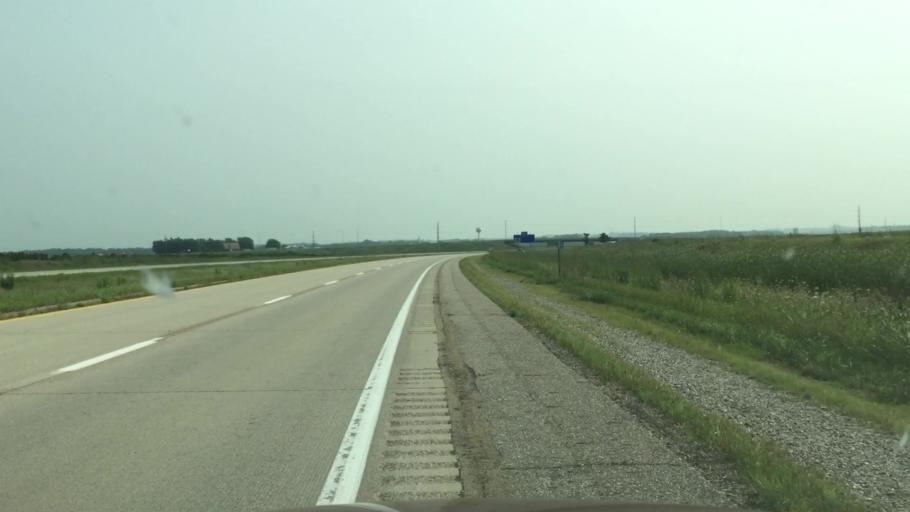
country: US
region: Iowa
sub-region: Osceola County
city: Sibley
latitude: 43.3782
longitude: -95.7573
